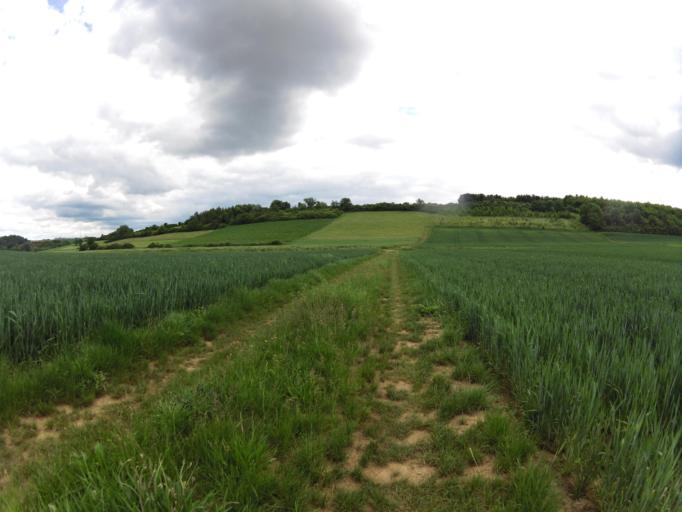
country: DE
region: Bavaria
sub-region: Regierungsbezirk Unterfranken
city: Gaukonigshofen
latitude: 49.6633
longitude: 10.0039
